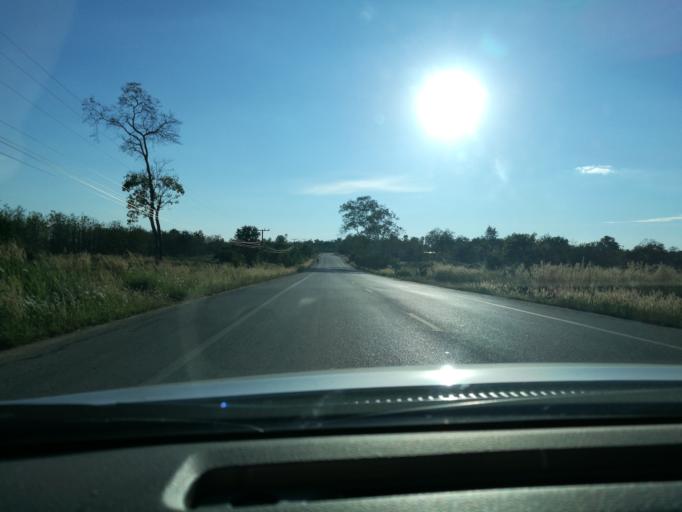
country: TH
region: Phitsanulok
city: Nakhon Thai
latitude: 17.0745
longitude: 100.8527
